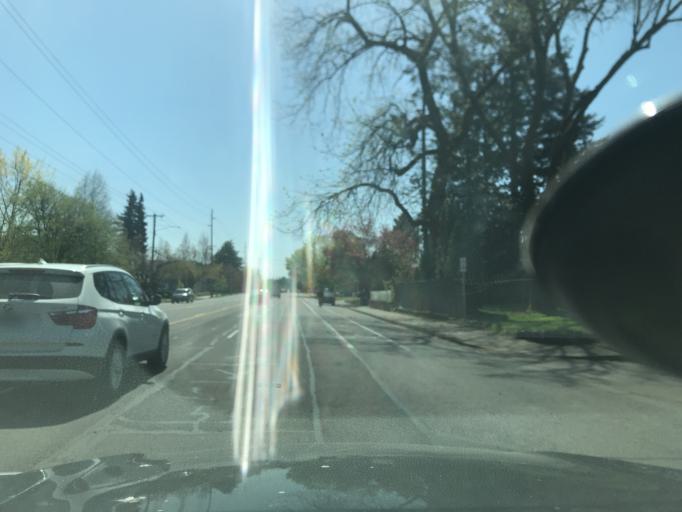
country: US
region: Oregon
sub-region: Multnomah County
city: Gresham
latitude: 45.5119
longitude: -122.4758
